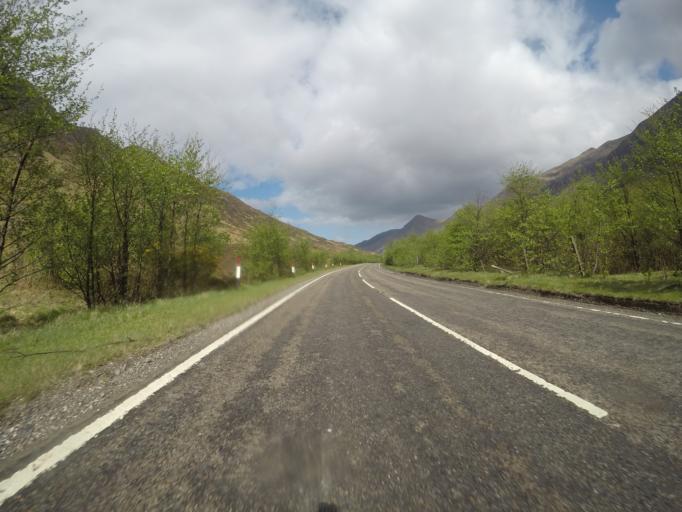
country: GB
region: Scotland
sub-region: Highland
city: Fort William
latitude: 57.1824
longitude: -5.3811
